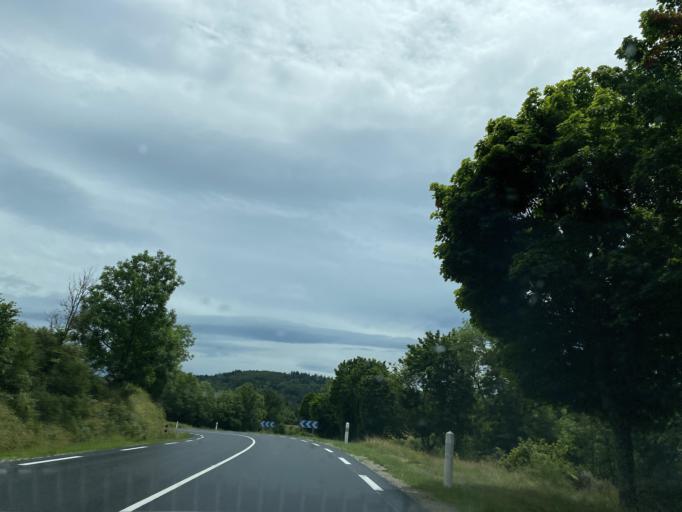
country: FR
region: Rhone-Alpes
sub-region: Departement de la Loire
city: Noiretable
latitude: 45.8142
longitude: 3.8141
